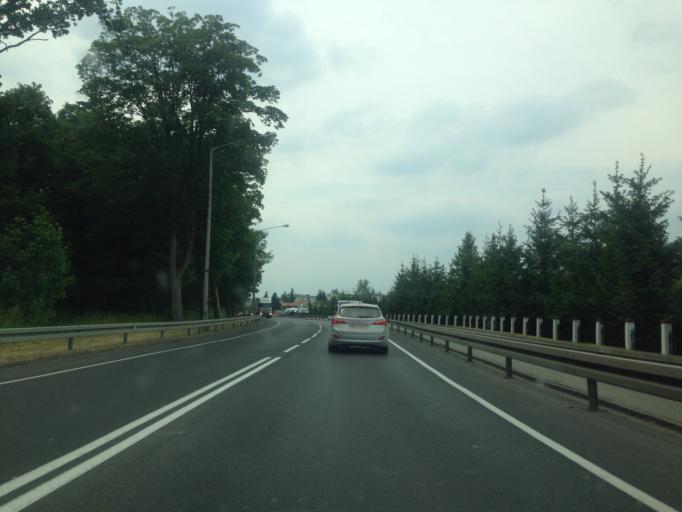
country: PL
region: Kujawsko-Pomorskie
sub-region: Grudziadz
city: Grudziadz
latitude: 53.5059
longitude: 18.8286
